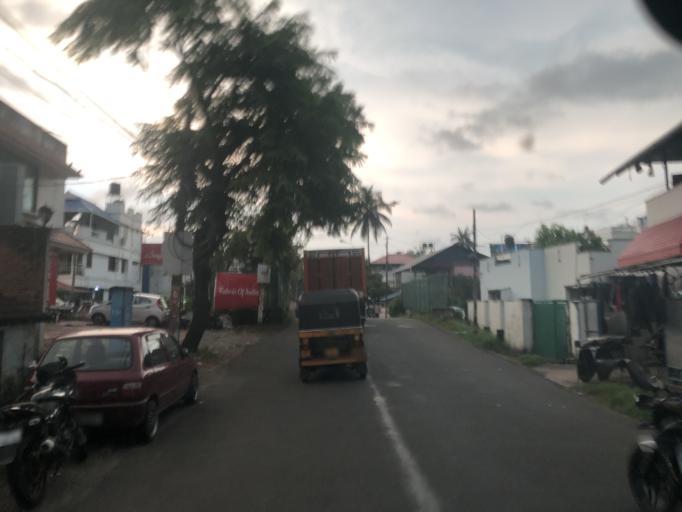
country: IN
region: Kerala
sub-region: Ernakulam
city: Cochin
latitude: 9.9522
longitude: 76.2474
